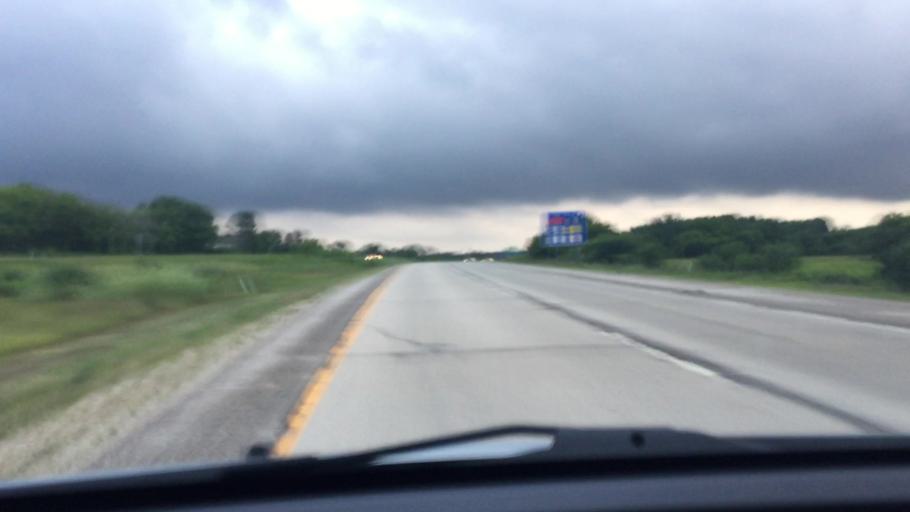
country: US
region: Wisconsin
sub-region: Walworth County
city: Lake Geneva
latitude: 42.5853
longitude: -88.3995
